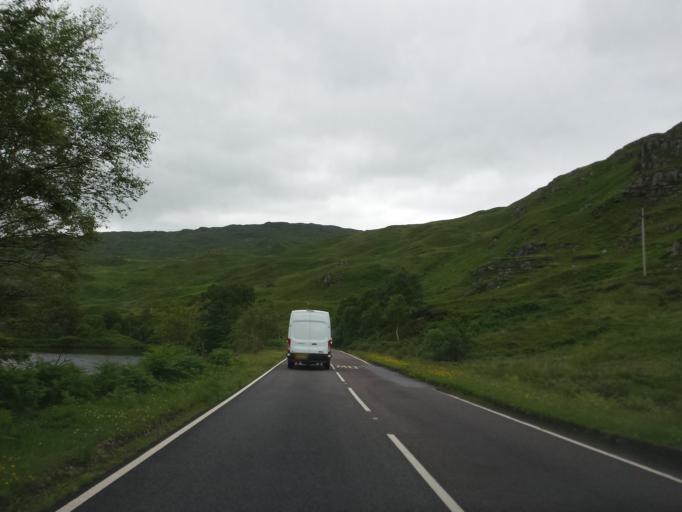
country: GB
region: Scotland
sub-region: Argyll and Bute
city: Isle Of Mull
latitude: 56.8839
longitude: -5.6141
